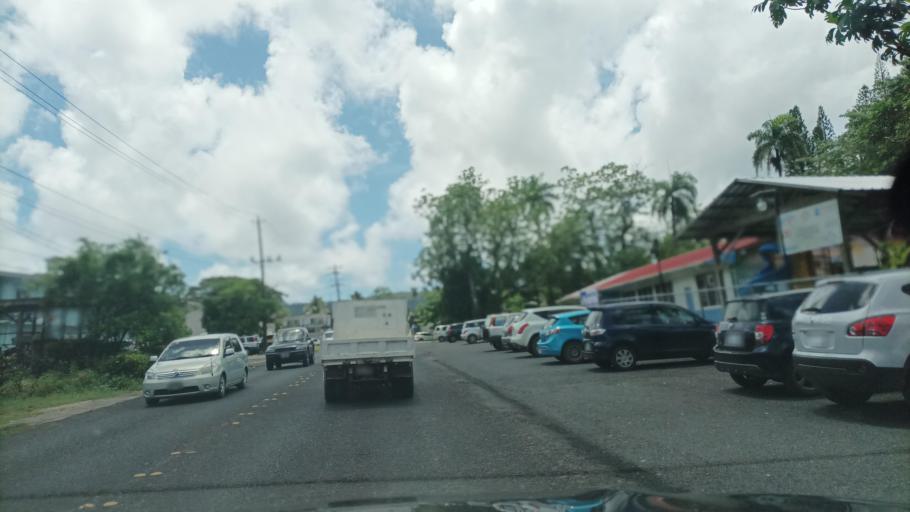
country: FM
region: Pohnpei
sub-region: Kolonia Municipality
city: Kolonia
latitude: 6.9584
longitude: 158.2087
